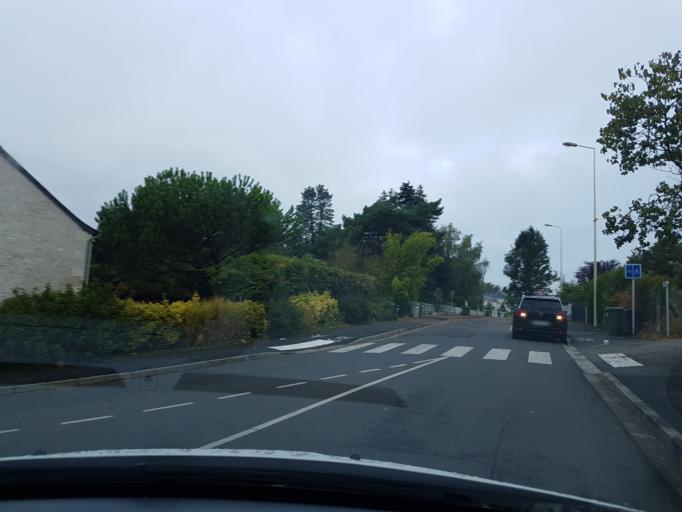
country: FR
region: Centre
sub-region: Departement d'Indre-et-Loire
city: Saint-Avertin
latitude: 47.3613
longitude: 0.7369
